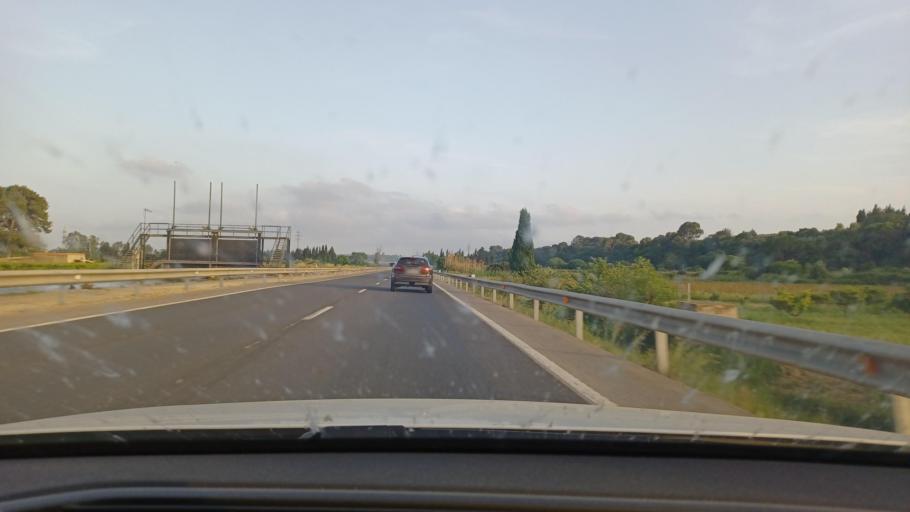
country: ES
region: Catalonia
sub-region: Provincia de Tarragona
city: Tortosa
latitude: 40.7703
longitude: 0.5297
